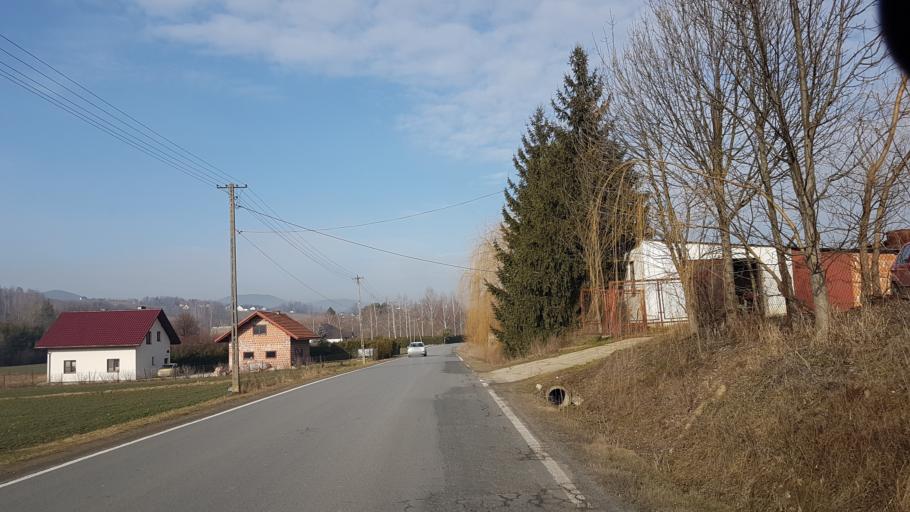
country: PL
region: Lesser Poland Voivodeship
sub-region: Powiat nowosadecki
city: Olszana
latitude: 49.5789
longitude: 20.5399
